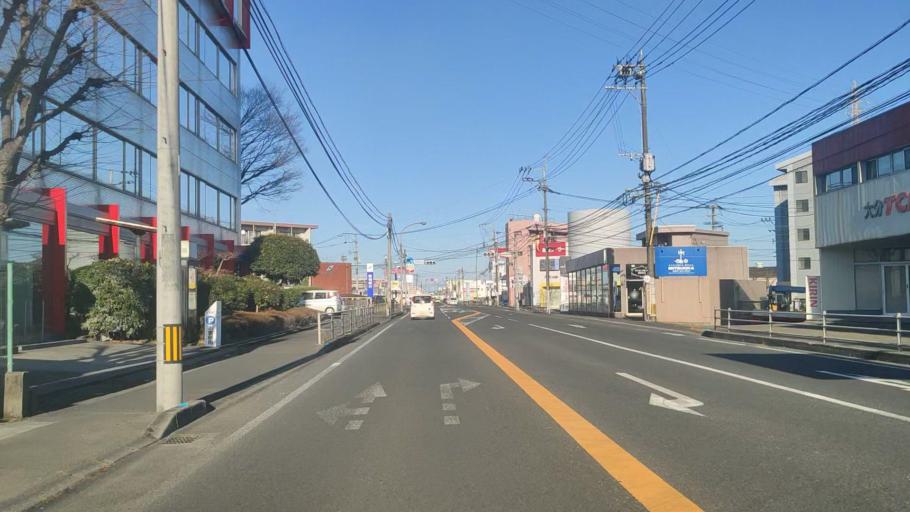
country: JP
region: Oita
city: Oita
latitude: 33.2170
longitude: 131.6132
